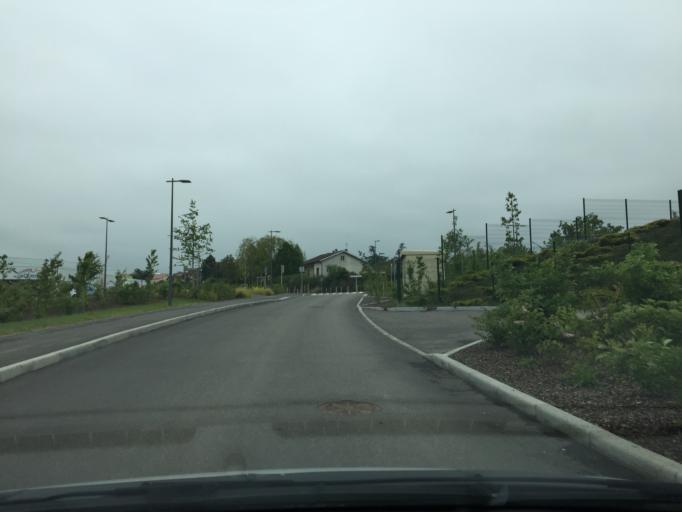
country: FR
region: Rhone-Alpes
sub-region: Departement du Rhone
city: Mornant
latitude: 45.6261
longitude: 4.6725
